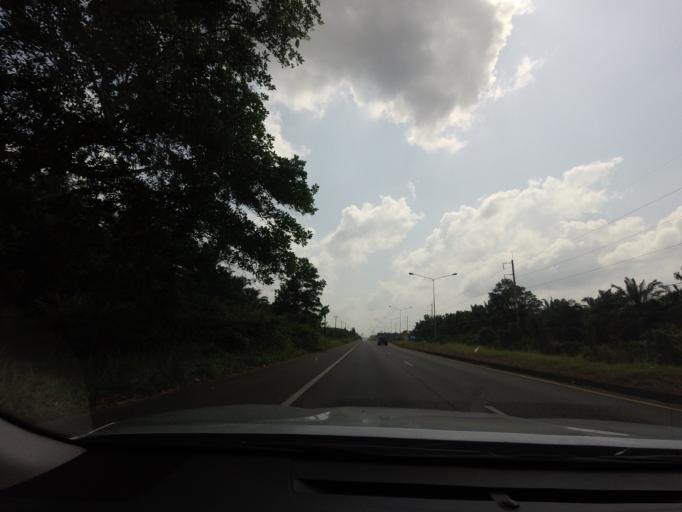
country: TH
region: Phangnga
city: Thap Put
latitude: 8.4990
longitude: 98.7021
